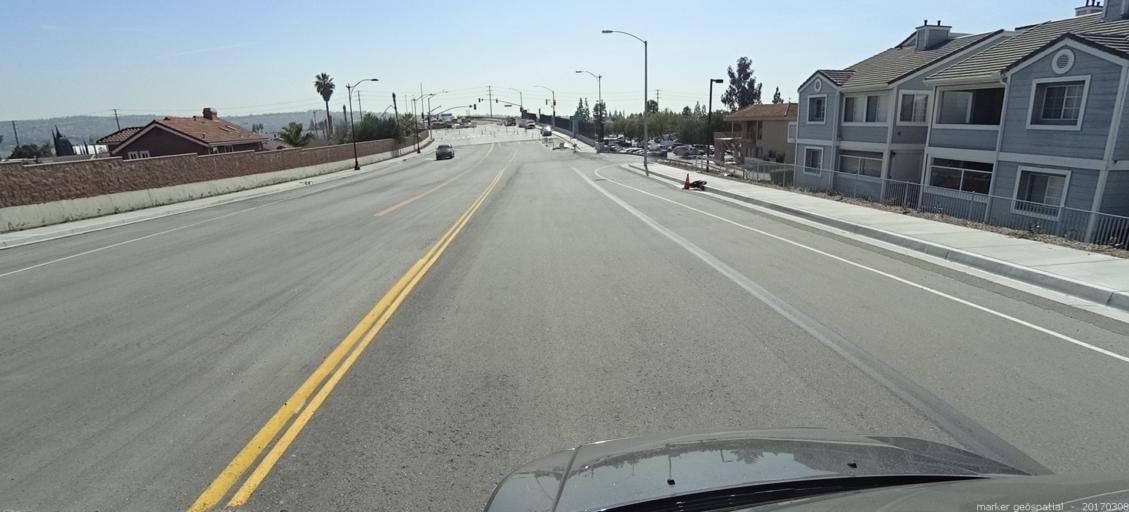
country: US
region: California
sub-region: Orange County
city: Yorba Linda
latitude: 33.8692
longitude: -117.8179
